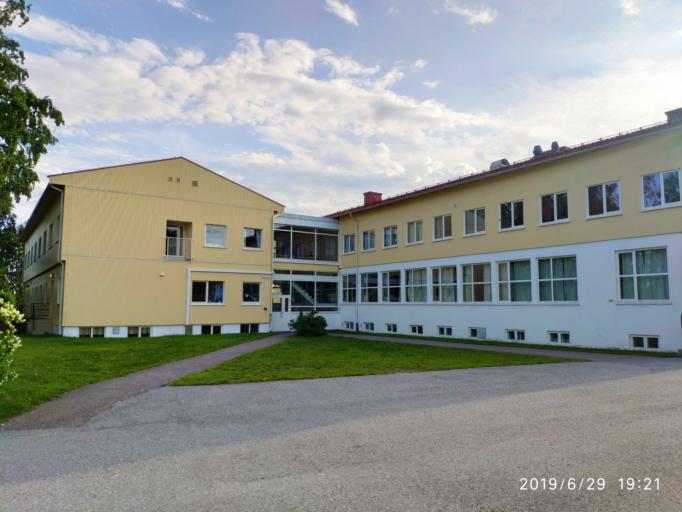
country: NO
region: Akershus
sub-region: Ullensaker
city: Jessheim
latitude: 60.1598
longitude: 11.1698
